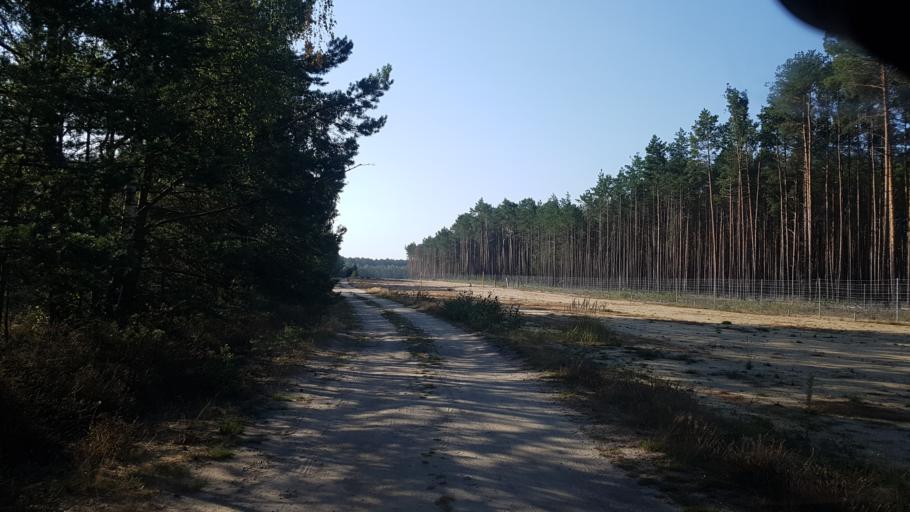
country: DE
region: Brandenburg
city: Finsterwalde
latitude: 51.6527
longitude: 13.6695
